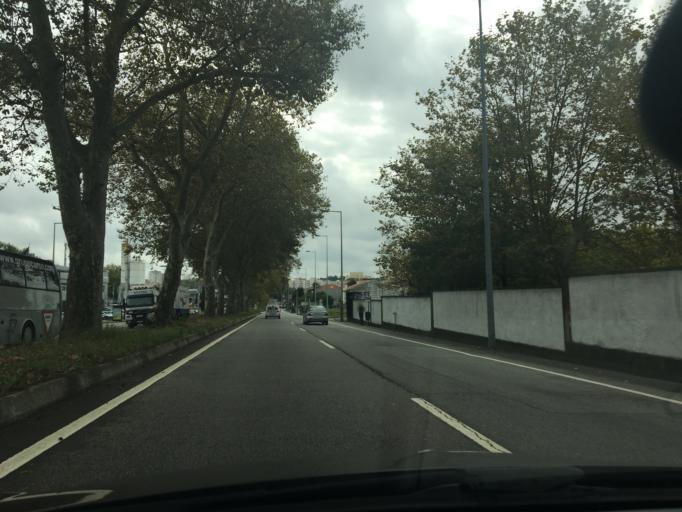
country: PT
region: Porto
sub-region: Matosinhos
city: Senhora da Hora
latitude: 41.1828
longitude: -8.6393
